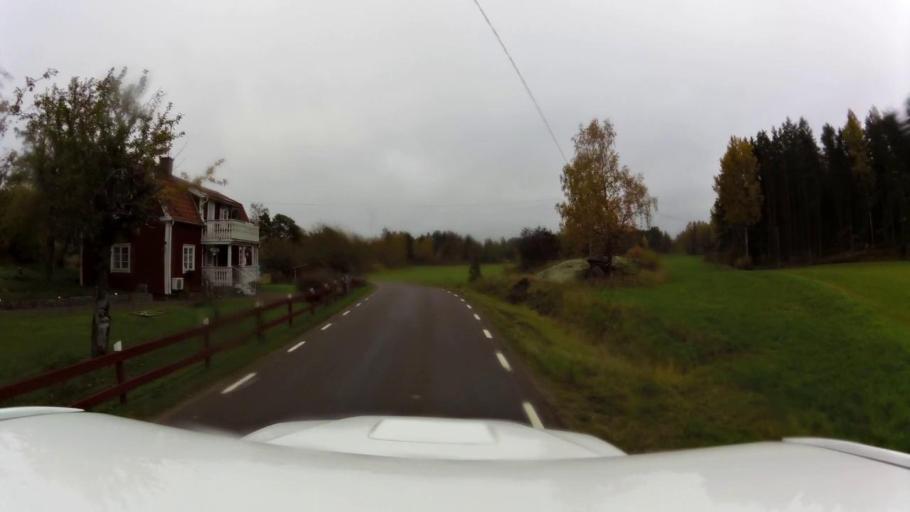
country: SE
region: OEstergoetland
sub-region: Linkopings Kommun
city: Linghem
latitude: 58.3521
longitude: 15.8622
